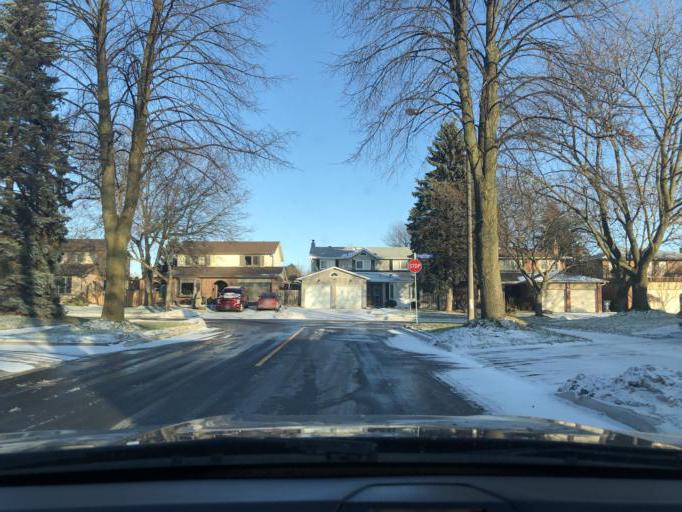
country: CA
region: Ontario
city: Scarborough
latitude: 43.7811
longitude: -79.1534
